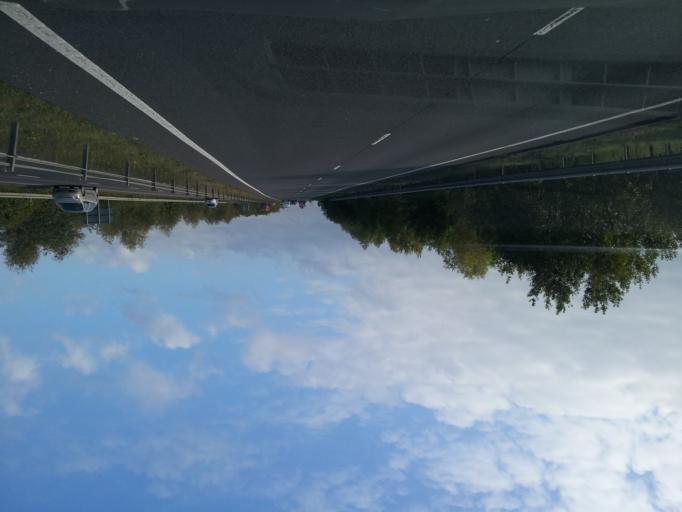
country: GB
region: England
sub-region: Northamptonshire
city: Brackley
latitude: 52.0579
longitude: -1.1057
